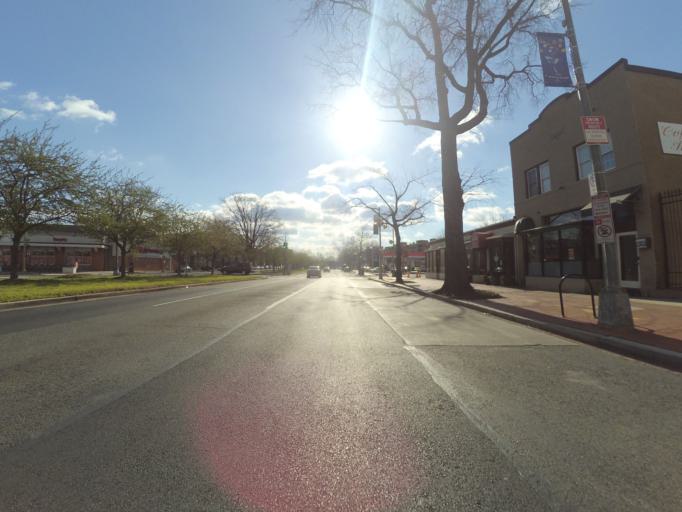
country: US
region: Washington, D.C.
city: Washington, D.C.
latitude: 38.8824
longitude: -76.9908
